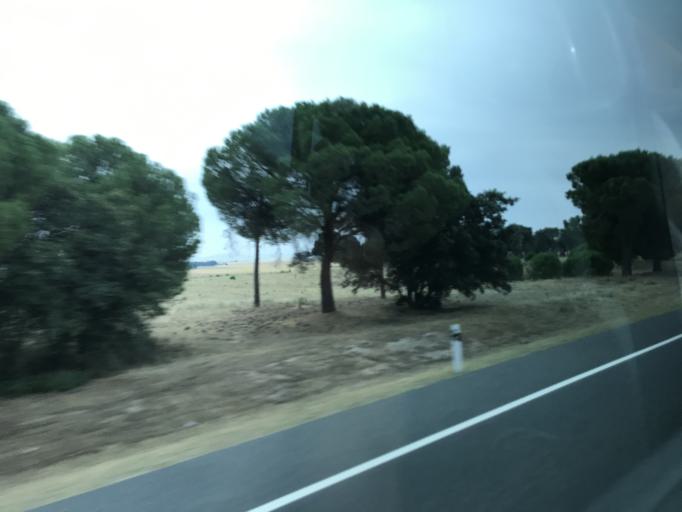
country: ES
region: Castille and Leon
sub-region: Provincia de Segovia
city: Rapariegos
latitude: 41.0694
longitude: -4.6330
